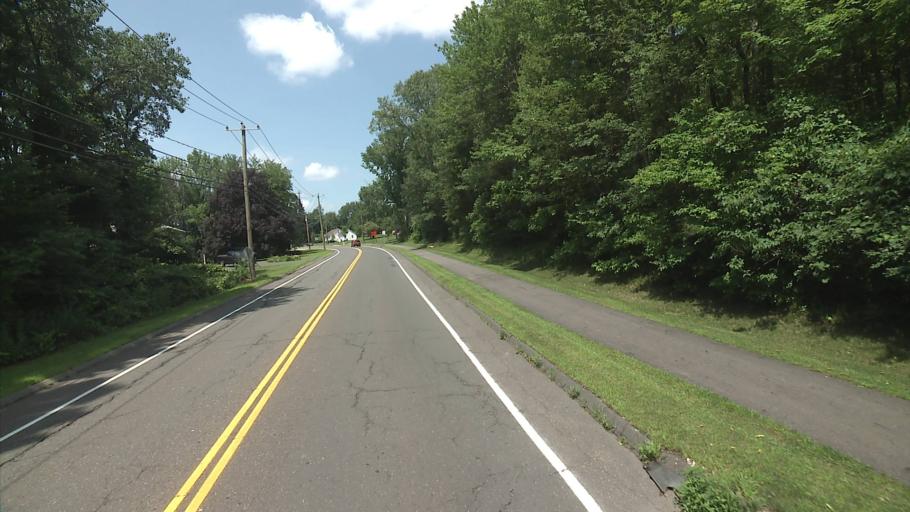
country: US
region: Connecticut
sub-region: Tolland County
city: South Coventry
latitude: 41.7754
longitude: -72.3080
